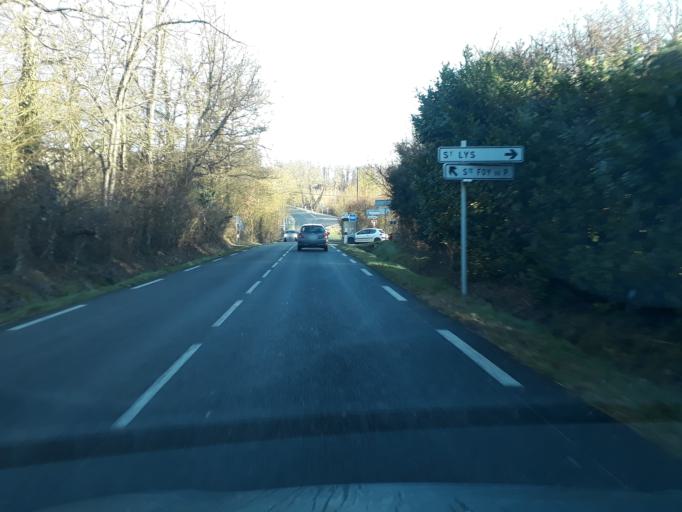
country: FR
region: Midi-Pyrenees
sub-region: Departement de la Haute-Garonne
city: Sainte-Foy-de-Peyrolieres
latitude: 43.4878
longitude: 1.1475
